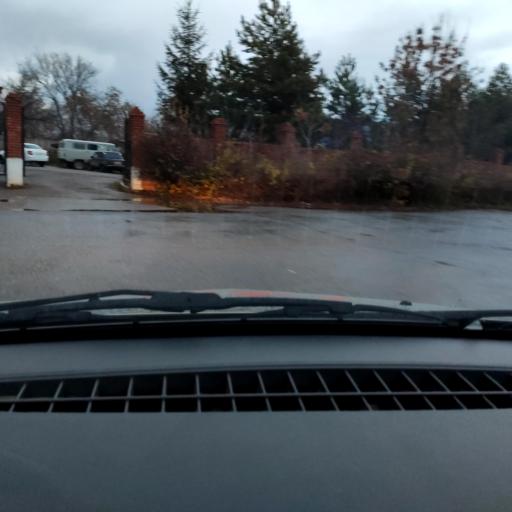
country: RU
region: Bashkortostan
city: Ufa
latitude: 54.7362
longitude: 55.9135
